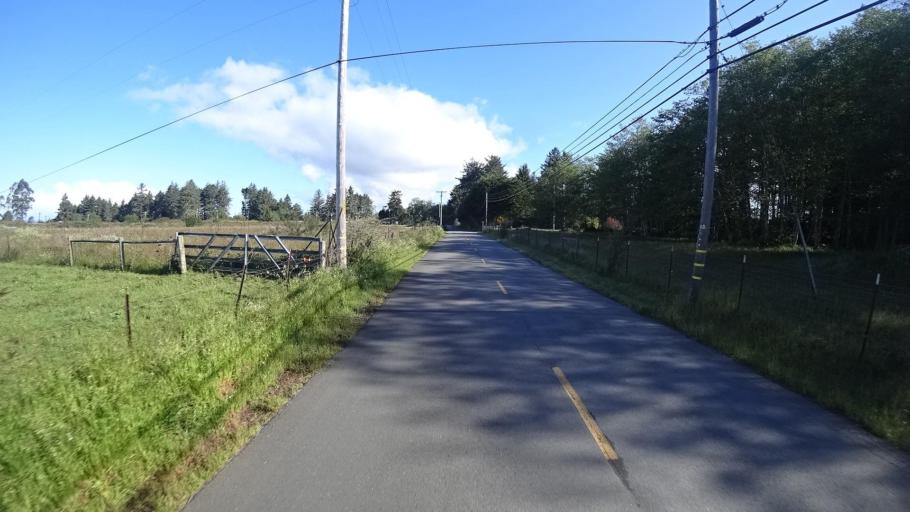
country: US
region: California
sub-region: Humboldt County
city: Westhaven-Moonstone
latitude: 41.0028
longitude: -124.1005
